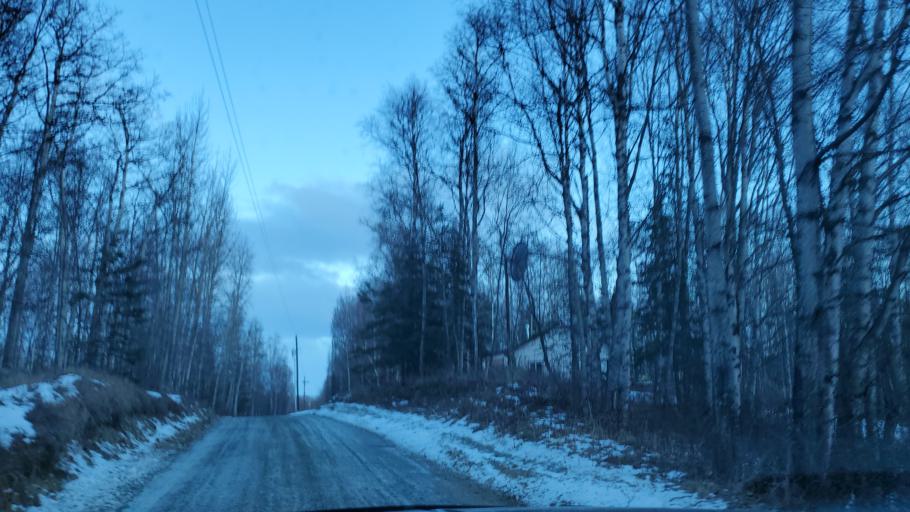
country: US
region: Alaska
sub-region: Matanuska-Susitna Borough
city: Lakes
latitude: 61.6633
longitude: -149.3269
